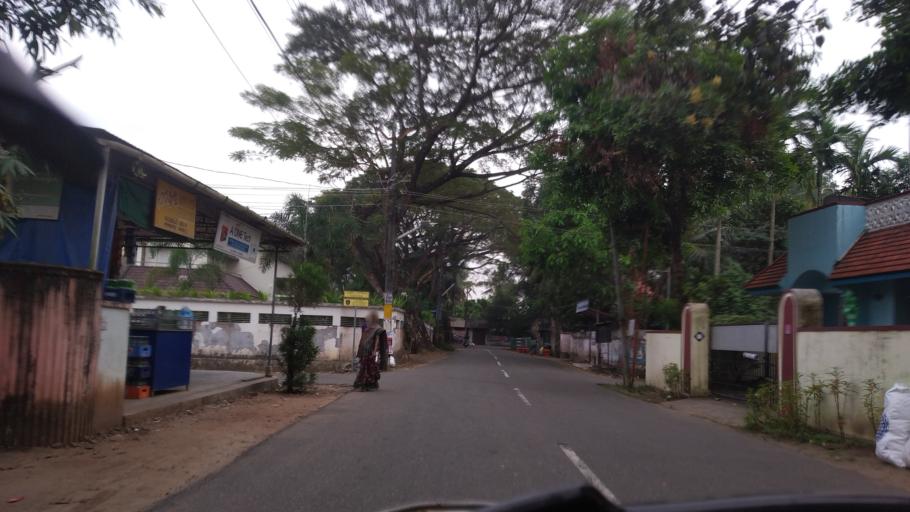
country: IN
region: Kerala
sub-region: Ernakulam
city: Elur
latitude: 10.1414
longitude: 76.2475
